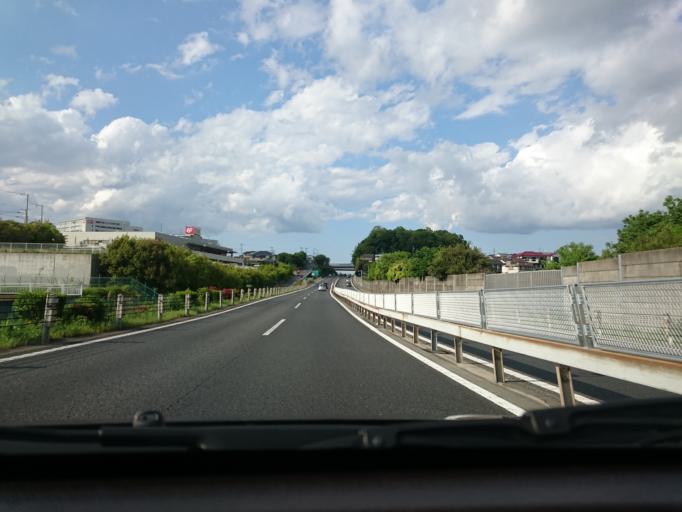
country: JP
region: Kanagawa
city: Isehara
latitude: 35.3488
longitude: 139.2977
